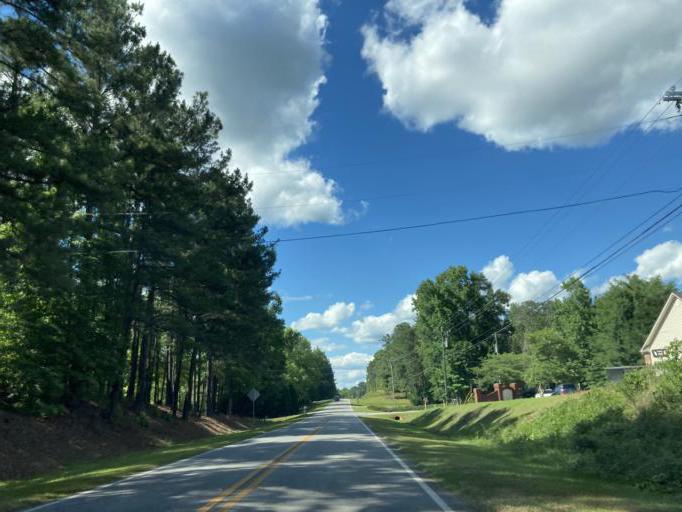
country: US
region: Georgia
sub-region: Jones County
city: Gray
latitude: 32.9868
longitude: -83.5504
